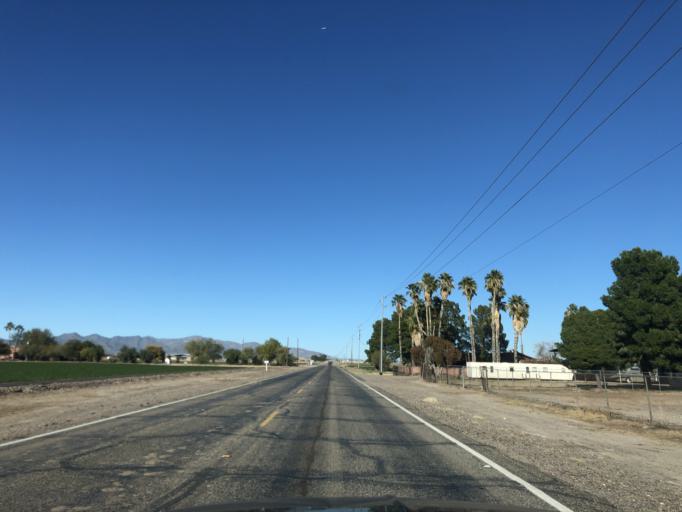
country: US
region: Arizona
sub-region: Maricopa County
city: Buckeye
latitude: 33.3816
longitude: -112.5042
